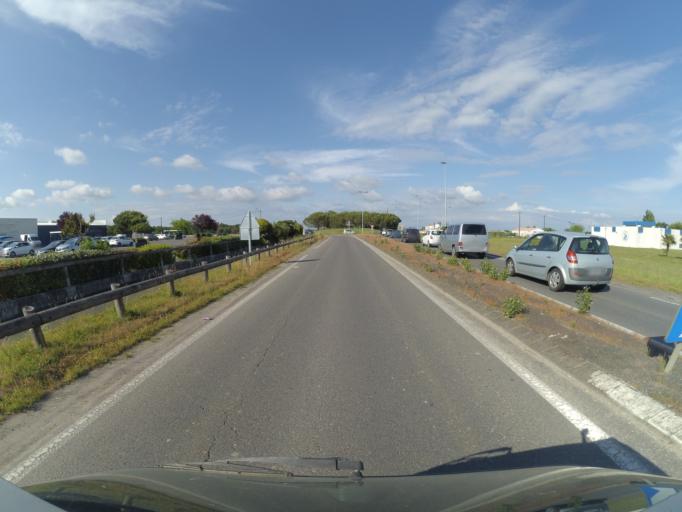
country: FR
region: Poitou-Charentes
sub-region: Departement de la Charente-Maritime
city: Le Gua
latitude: 45.7310
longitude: -0.9571
